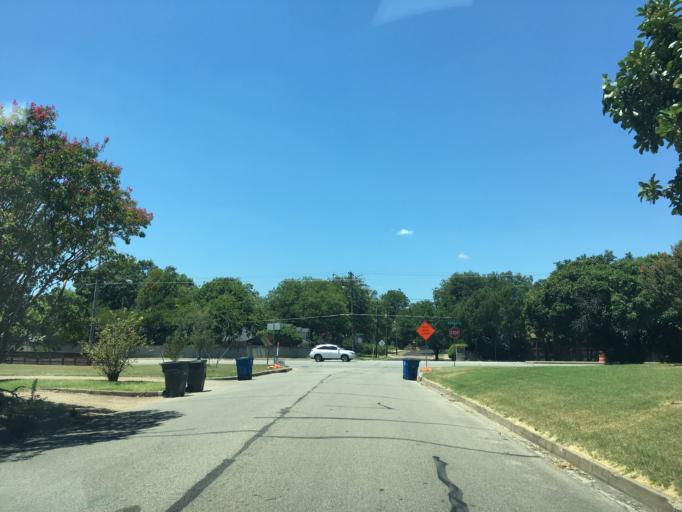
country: US
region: Texas
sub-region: Dallas County
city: Highland Park
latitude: 32.8352
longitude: -96.6994
